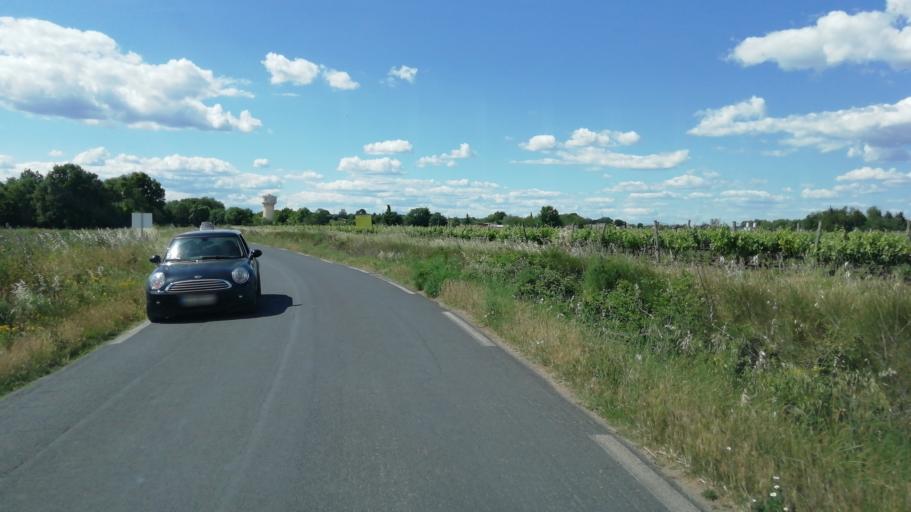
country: FR
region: Languedoc-Roussillon
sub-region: Departement de l'Herault
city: Lunel-Viel
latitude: 43.6703
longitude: 4.1028
